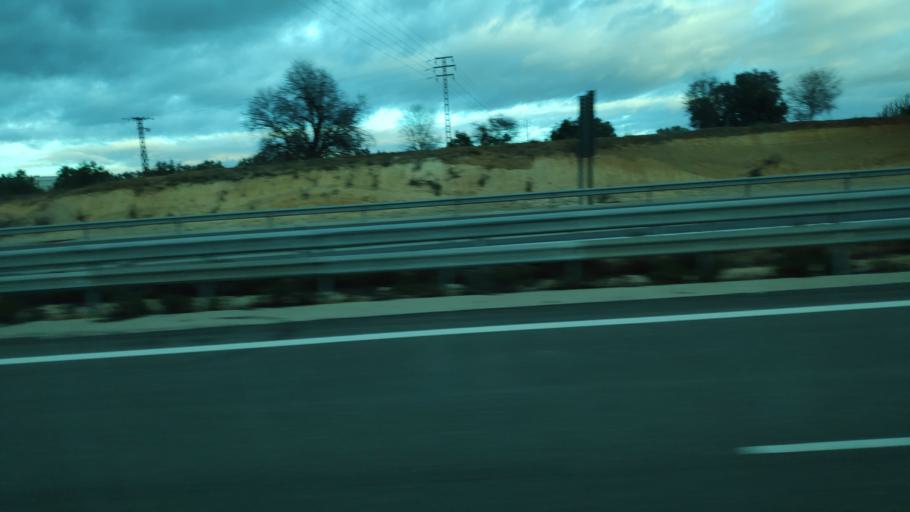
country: ES
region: Castille-La Mancha
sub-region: Provincia de Cuenca
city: Tarancon
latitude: 40.0120
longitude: -3.0299
